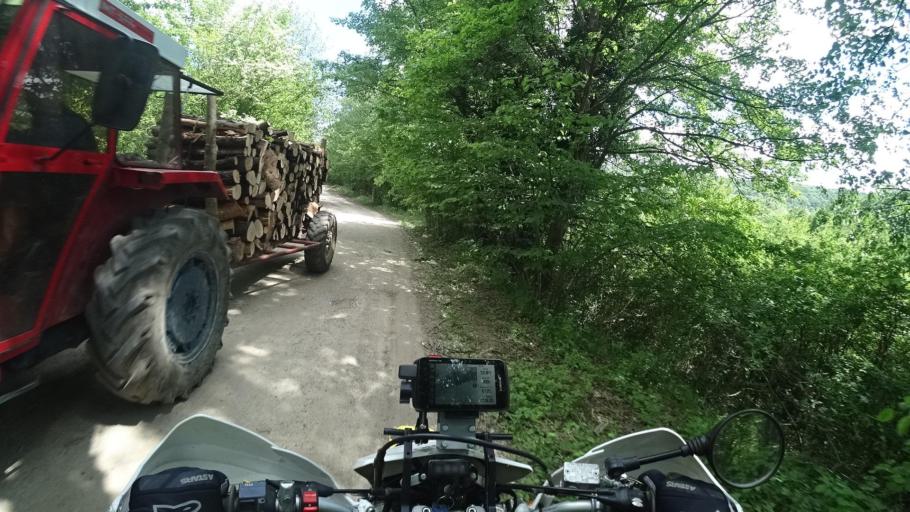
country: BA
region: Federation of Bosnia and Herzegovina
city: Ostrozac
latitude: 44.8316
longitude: 15.9758
